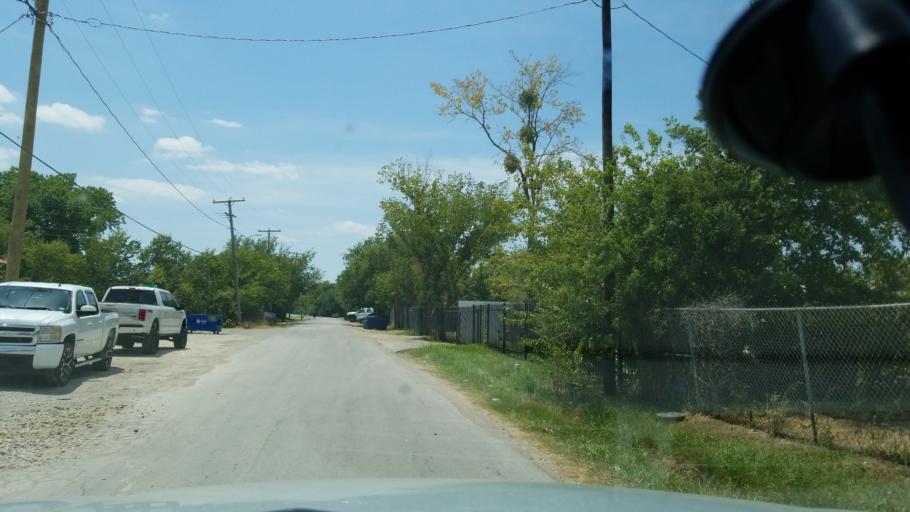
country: US
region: Texas
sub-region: Dallas County
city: Grand Prairie
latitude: 32.7485
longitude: -96.9731
